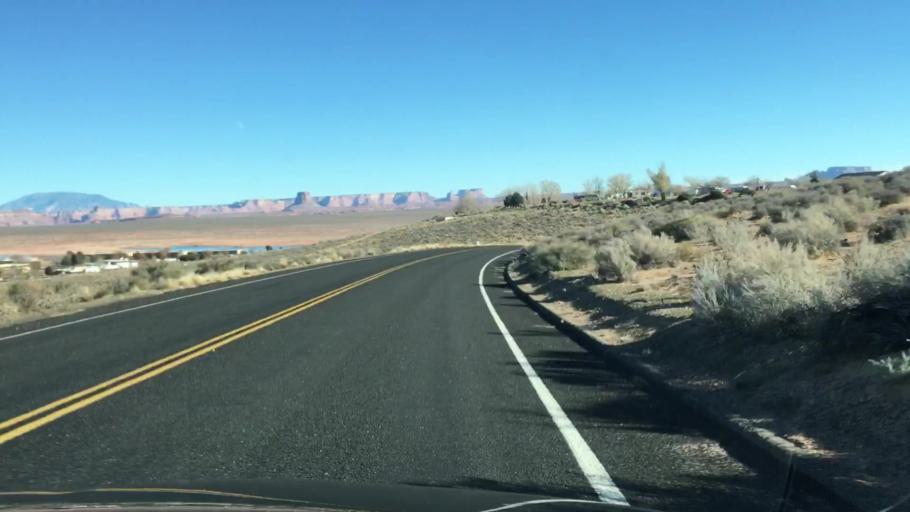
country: US
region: Arizona
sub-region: Coconino County
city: Page
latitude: 36.9941
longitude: -111.4985
